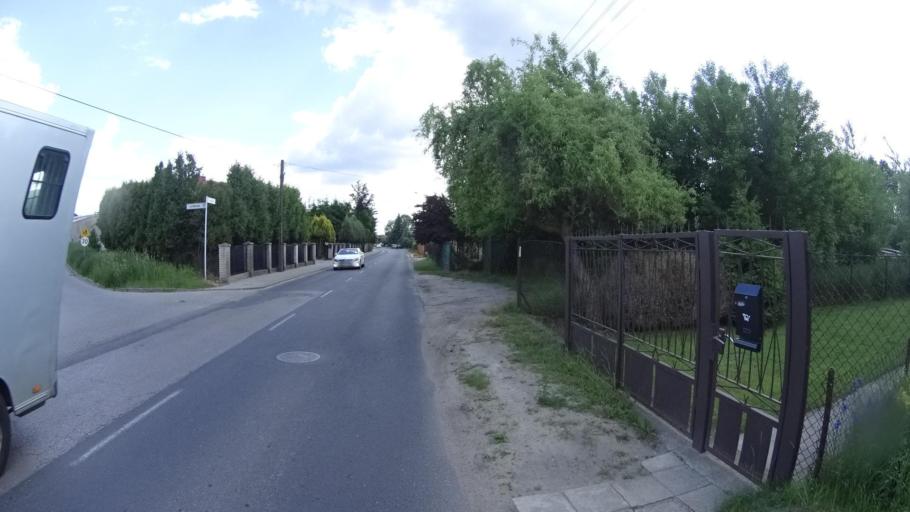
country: PL
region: Masovian Voivodeship
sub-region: Powiat piaseczynski
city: Tarczyn
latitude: 51.9833
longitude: 20.8305
